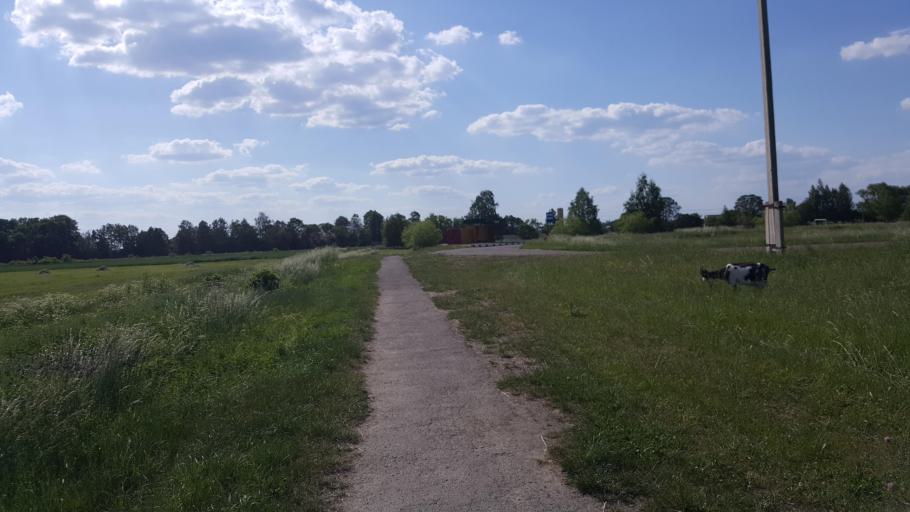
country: BY
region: Brest
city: Kobryn
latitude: 52.3394
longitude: 24.2411
